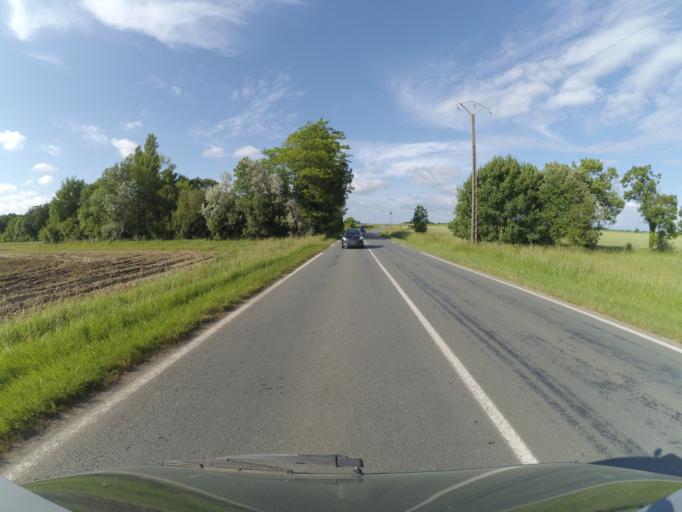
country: FR
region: Poitou-Charentes
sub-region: Departement de la Charente-Maritime
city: Le Gua
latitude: 45.7328
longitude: -0.9554
